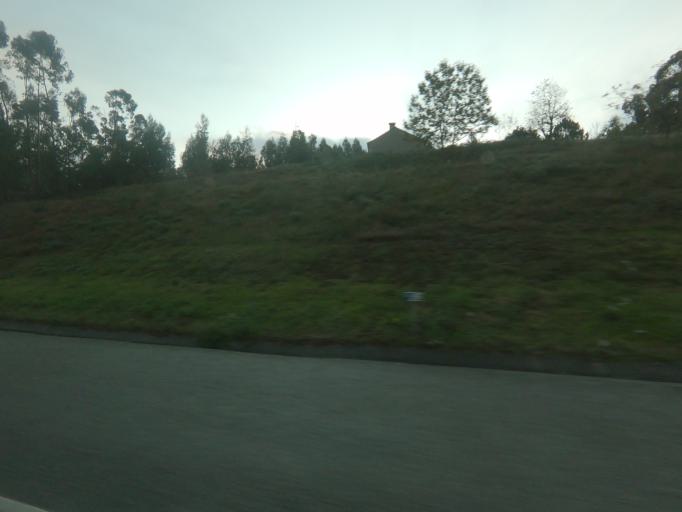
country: PT
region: Braga
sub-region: Vila Verde
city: Prado
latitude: 41.6680
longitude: -8.5471
